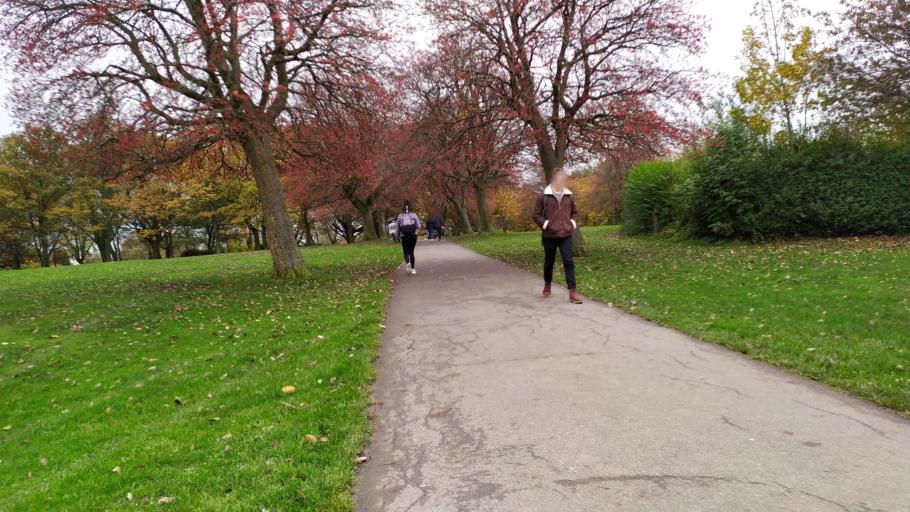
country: GB
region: England
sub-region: City and Borough of Leeds
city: Leeds
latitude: 53.8114
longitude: -1.5623
